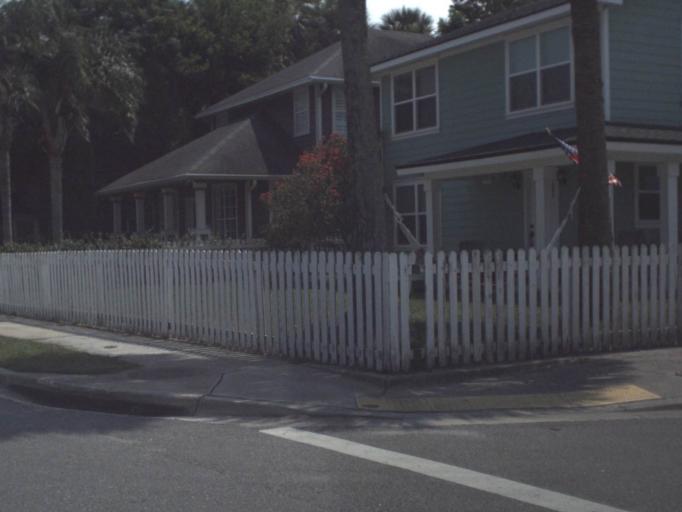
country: US
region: Florida
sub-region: Duval County
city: Neptune Beach
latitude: 30.3092
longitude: -81.3961
